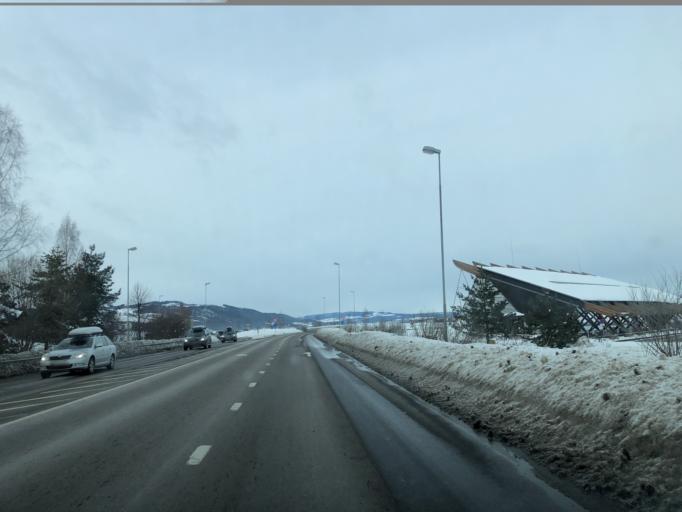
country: NO
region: Oppland
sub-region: Gjovik
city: Gjovik
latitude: 60.7971
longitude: 10.6963
